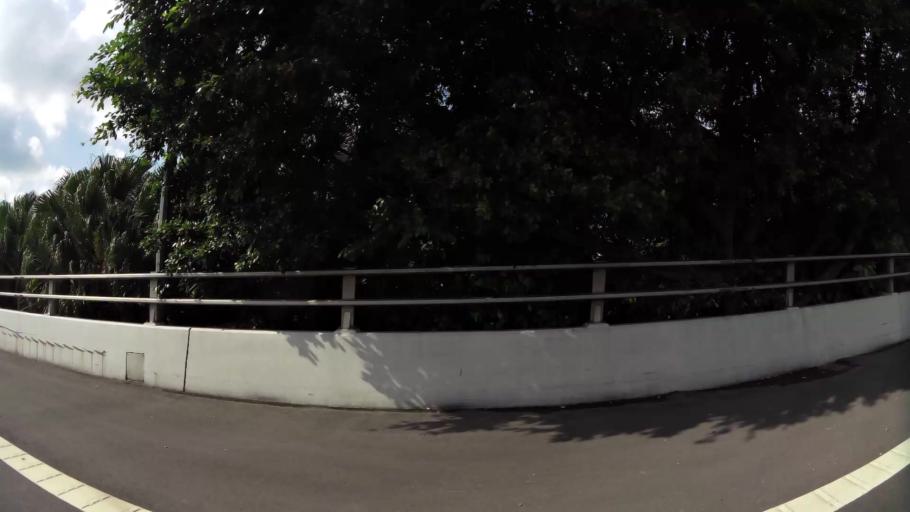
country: SG
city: Singapore
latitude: 1.2736
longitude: 103.8305
